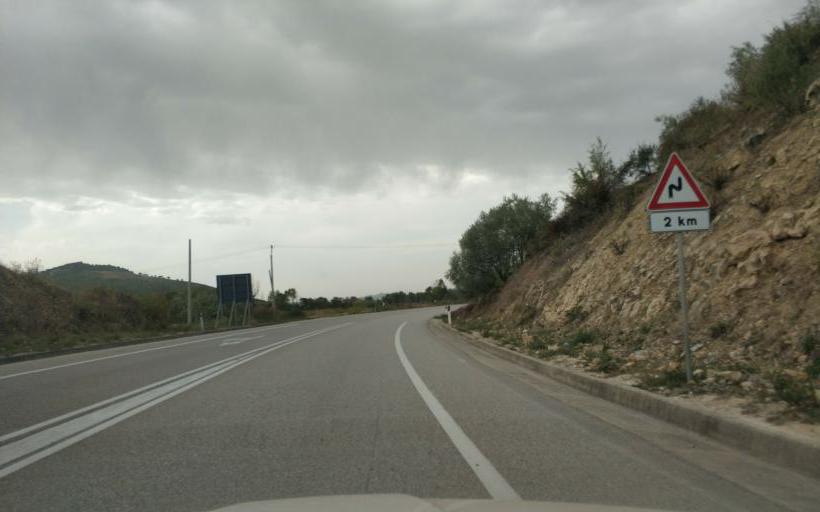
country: AL
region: Fier
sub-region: Rrethi i Mallakastres
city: Kute
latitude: 40.5148
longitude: 19.7443
